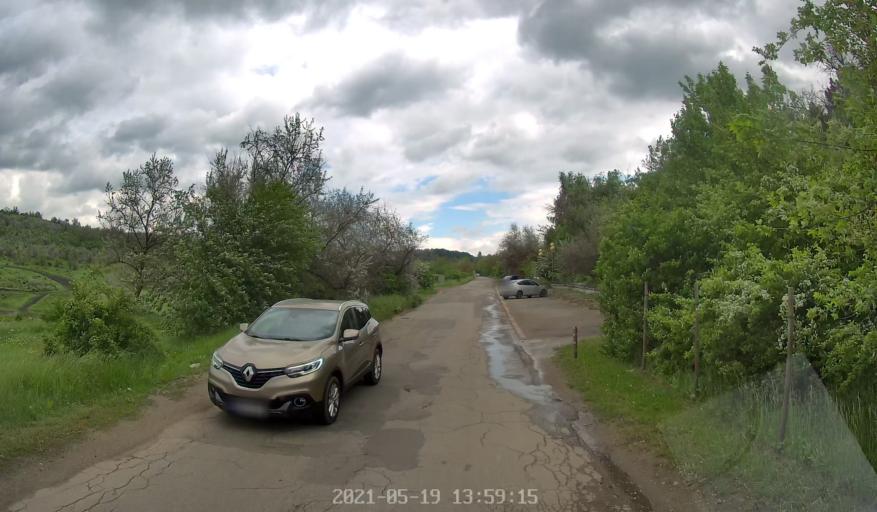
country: MD
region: Chisinau
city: Chisinau
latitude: 47.0412
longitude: 28.9223
